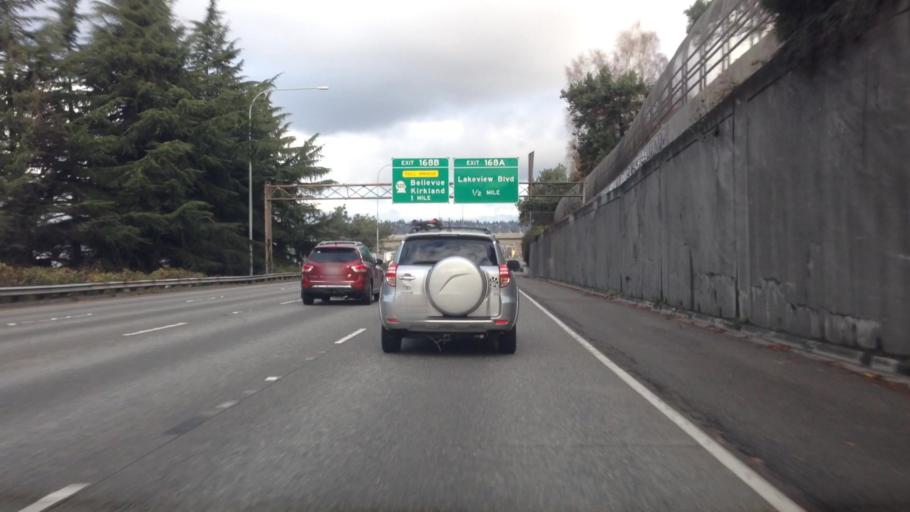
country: US
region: Washington
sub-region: King County
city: Seattle
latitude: 47.6255
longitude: -122.3281
